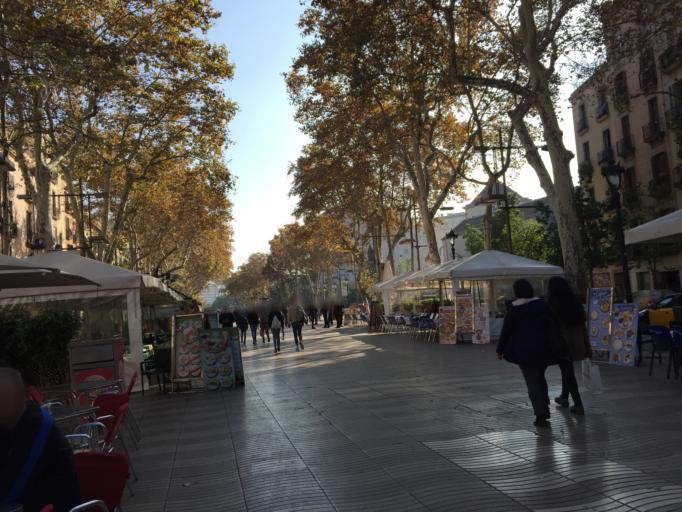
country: ES
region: Catalonia
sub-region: Provincia de Barcelona
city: Ciutat Vella
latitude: 41.3782
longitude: 2.1759
